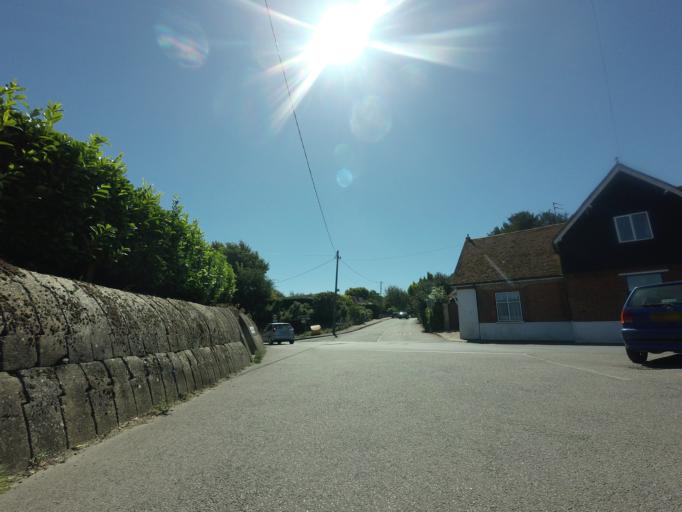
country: GB
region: England
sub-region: Kent
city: Eastry
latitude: 51.2645
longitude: 1.3059
